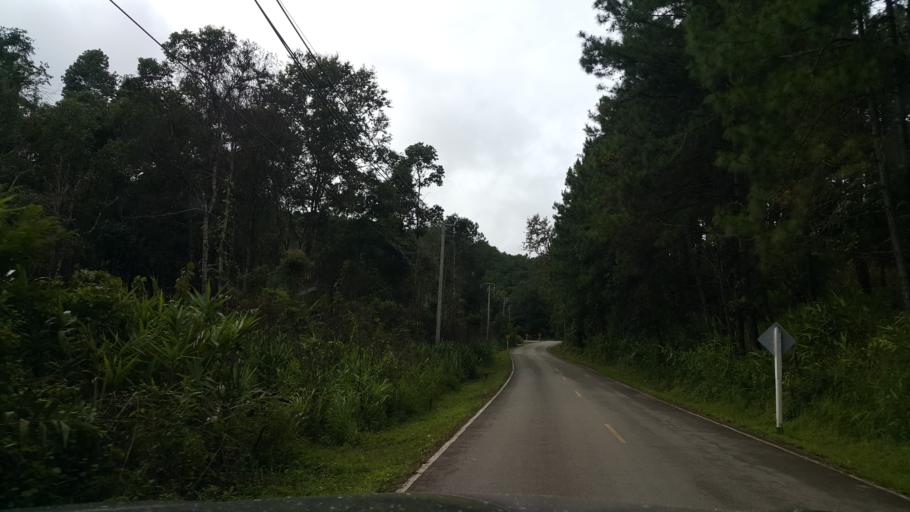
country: TH
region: Chiang Mai
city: Samoeng
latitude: 18.8867
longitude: 98.5012
